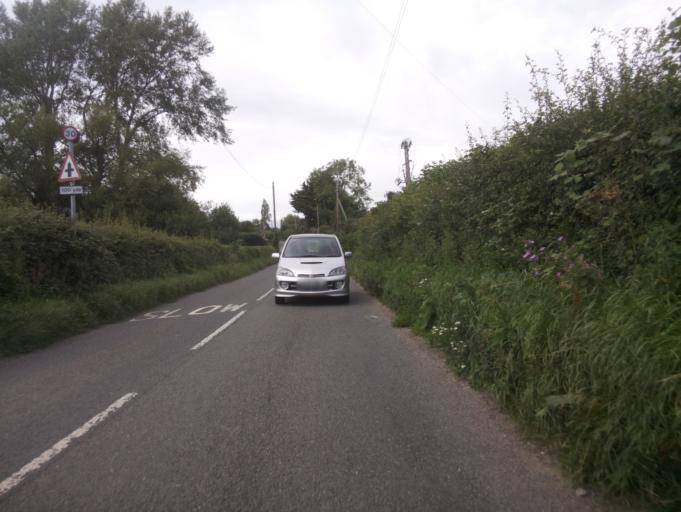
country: GB
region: England
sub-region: Somerset
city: Street
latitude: 51.1126
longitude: -2.7041
